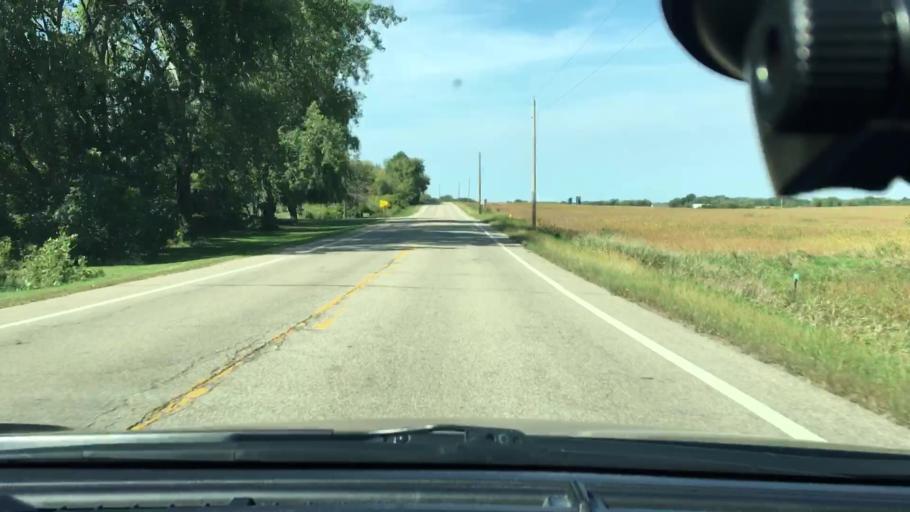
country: US
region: Minnesota
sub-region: Hennepin County
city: Corcoran
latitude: 45.1161
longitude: -93.5897
